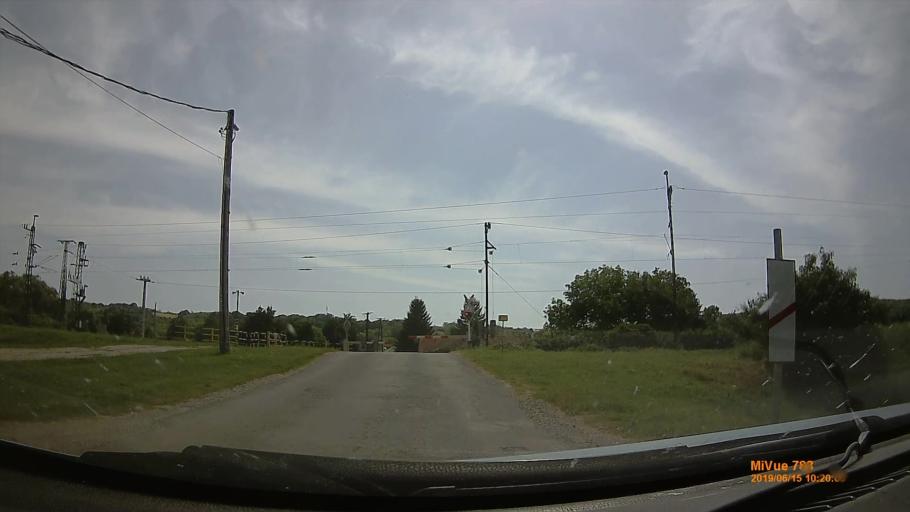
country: HU
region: Baranya
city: Buekkoesd
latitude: 46.1107
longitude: 17.9977
